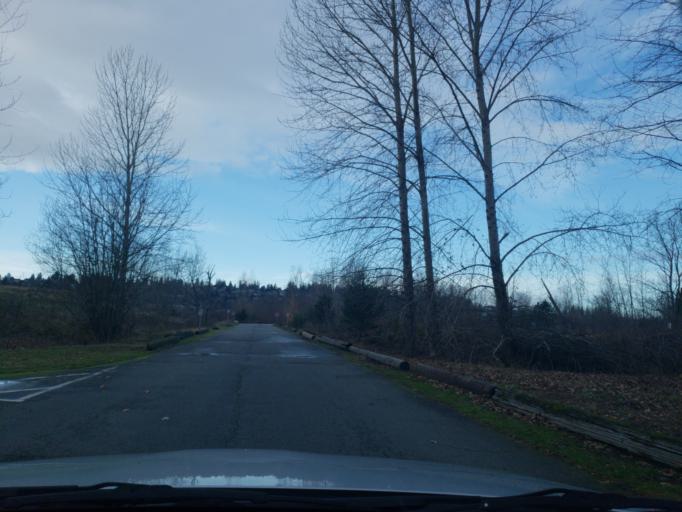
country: US
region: Washington
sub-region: King County
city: Kirkland
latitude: 47.6771
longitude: -122.2510
